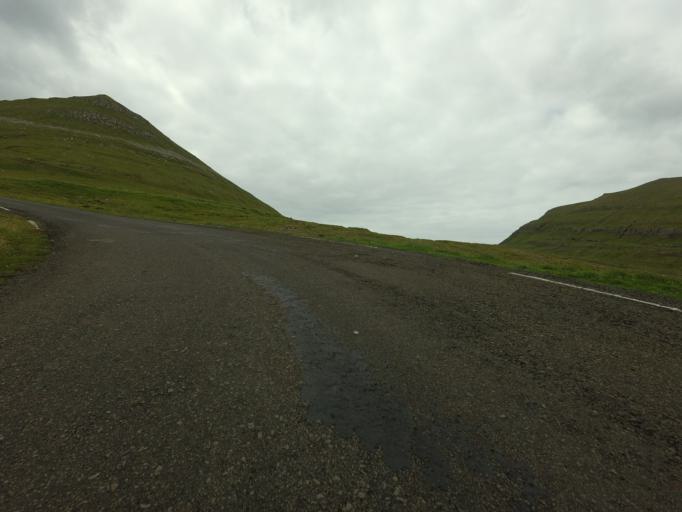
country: FO
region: Suduroy
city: Vagur
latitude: 61.4418
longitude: -6.7765
